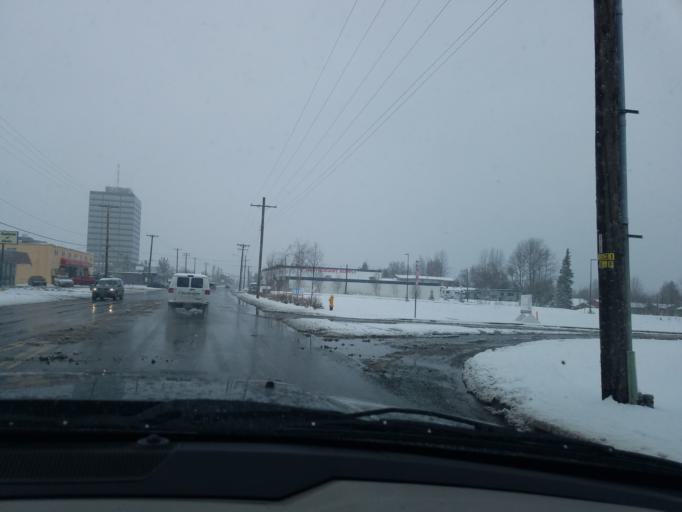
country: US
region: Alaska
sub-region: Anchorage Municipality
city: Anchorage
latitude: 61.1979
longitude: -149.8701
